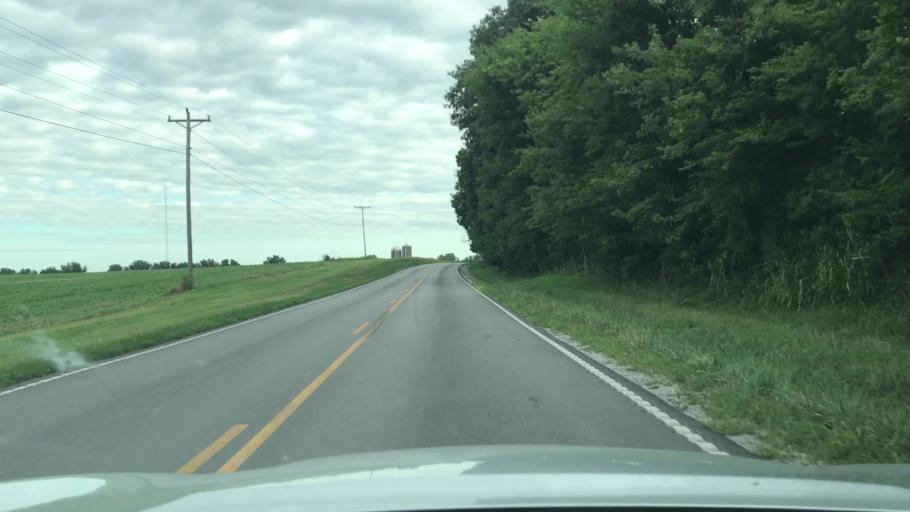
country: US
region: Kentucky
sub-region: Todd County
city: Guthrie
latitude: 36.6907
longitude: -87.2011
